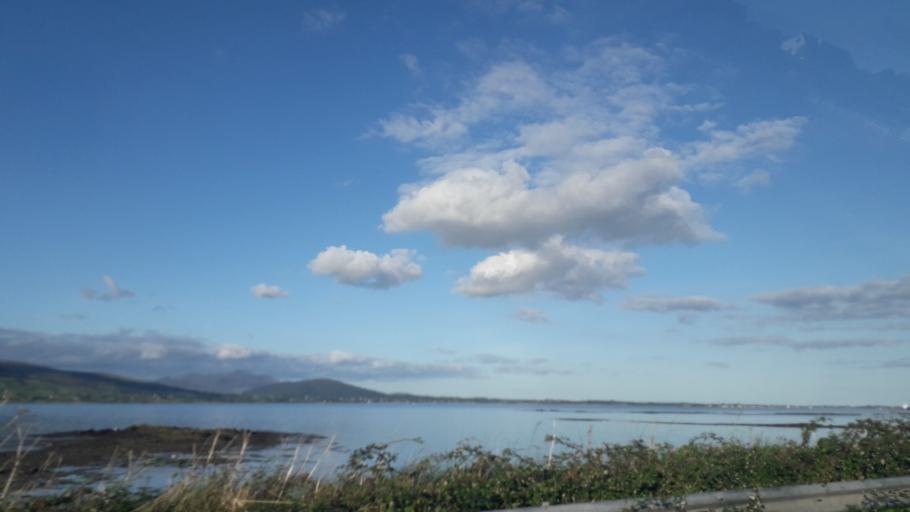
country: IE
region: Leinster
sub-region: Lu
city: Carlingford
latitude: 54.0367
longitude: -6.1712
